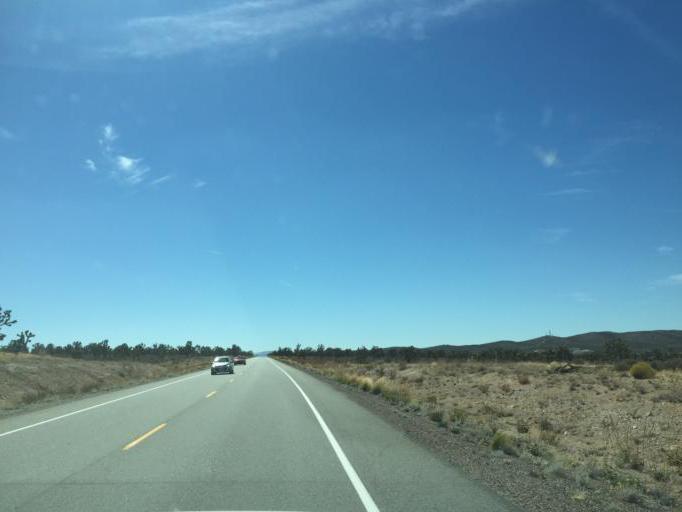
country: US
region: Arizona
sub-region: Mohave County
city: Meadview
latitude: 35.8742
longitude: -114.0603
